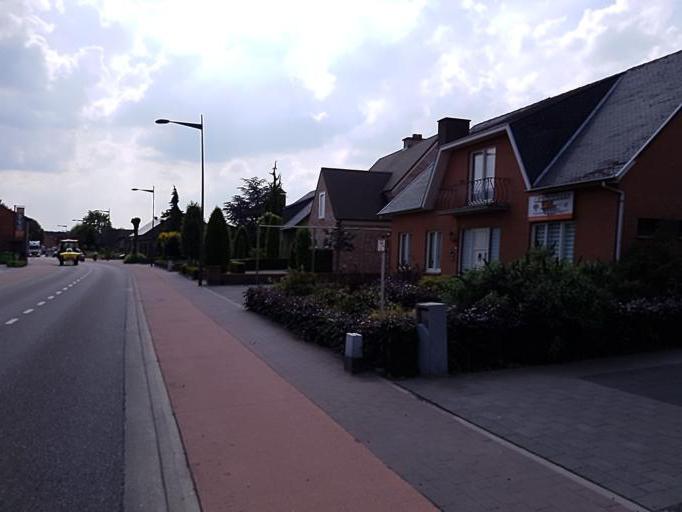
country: NL
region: North Brabant
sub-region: Gemeente Cranendonck
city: Cranendonck
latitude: 51.2495
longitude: 5.5378
